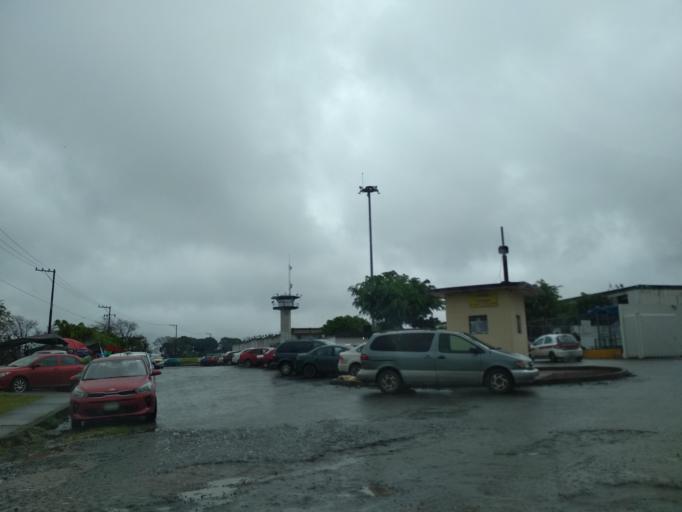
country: MX
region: Veracruz
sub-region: Amatlan de los Reyes
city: Centro de Readaptacion Social
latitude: 18.8384
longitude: -96.9396
